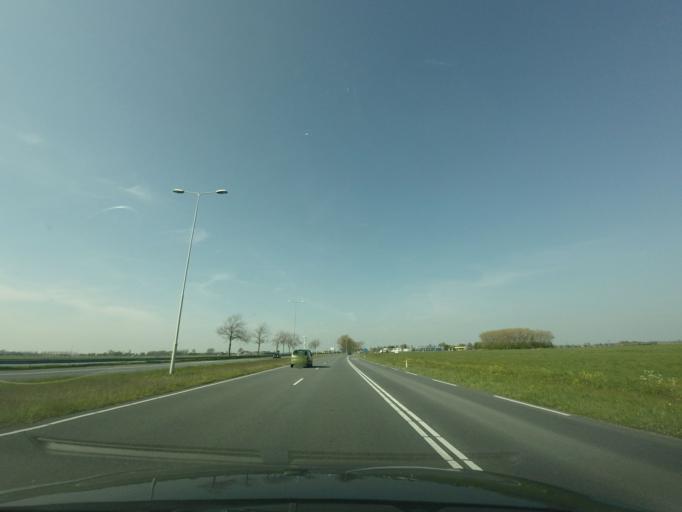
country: NL
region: North Holland
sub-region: Gemeente Landsmeer
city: Landsmeer
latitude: 52.4165
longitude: 4.9465
